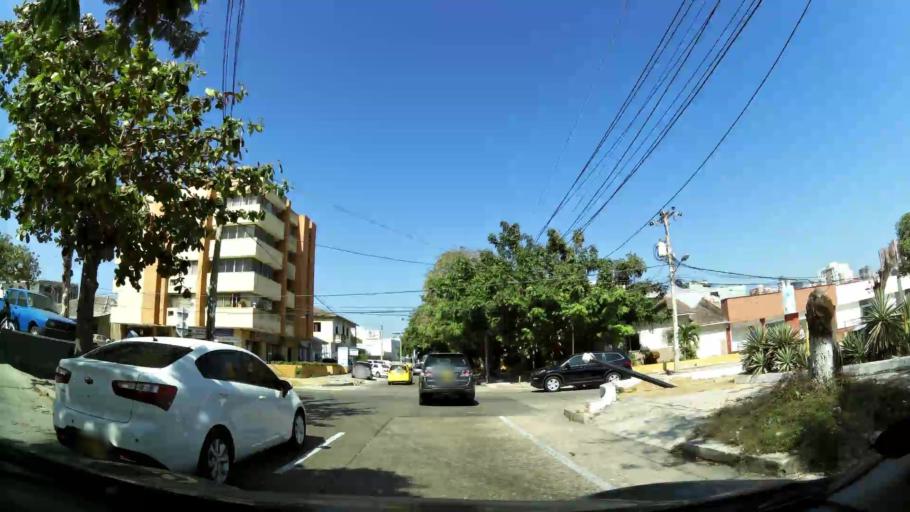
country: CO
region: Atlantico
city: Barranquilla
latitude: 10.9968
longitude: -74.8084
